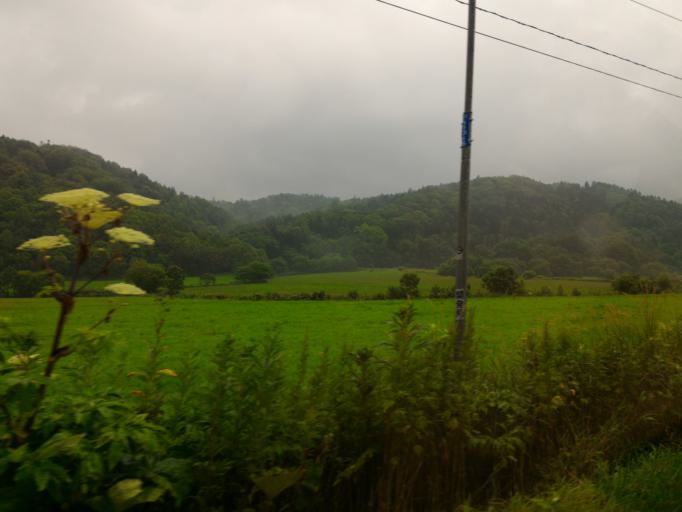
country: JP
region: Hokkaido
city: Nayoro
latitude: 44.6150
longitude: 142.3063
